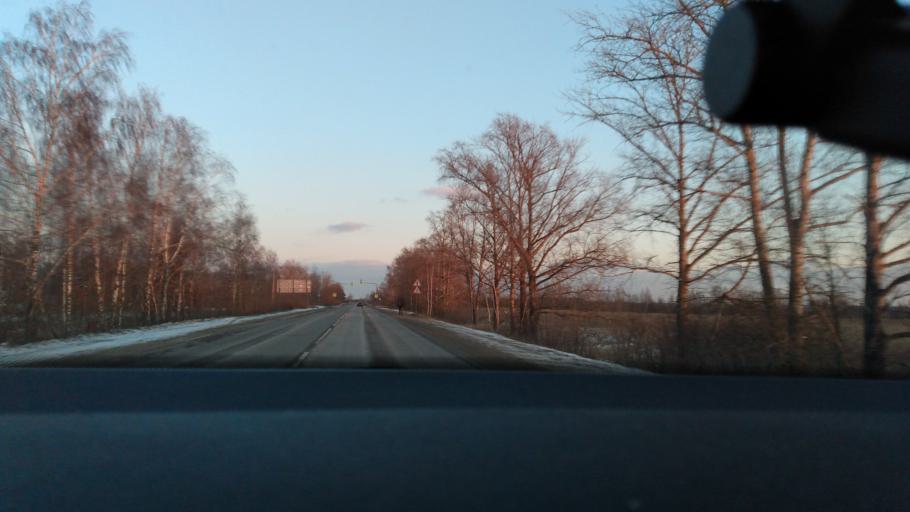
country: RU
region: Moskovskaya
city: Kolomna
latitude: 55.0885
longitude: 38.9135
